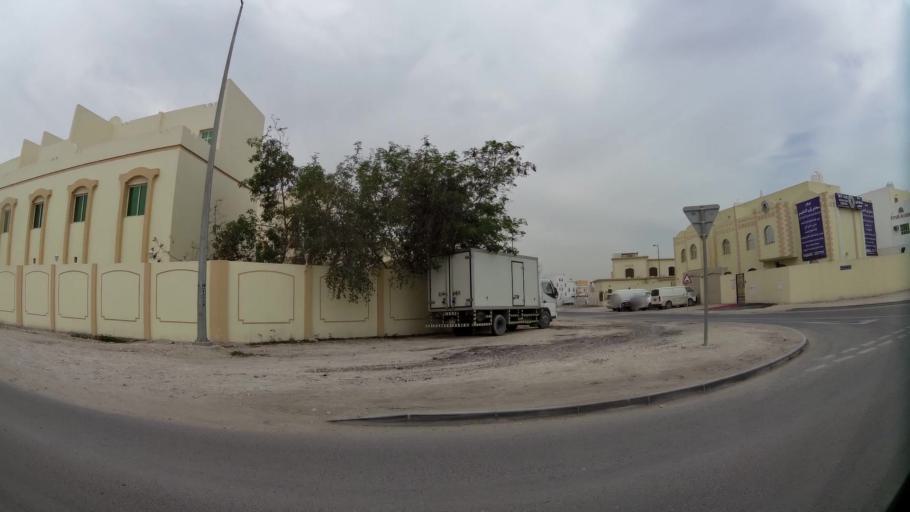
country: QA
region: Baladiyat ad Dawhah
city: Doha
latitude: 25.2222
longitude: 51.4738
